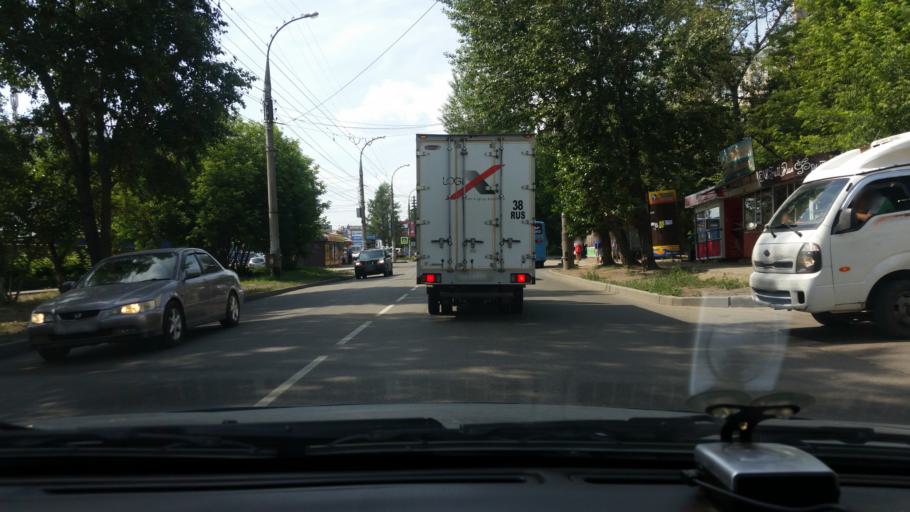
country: RU
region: Irkutsk
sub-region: Irkutskiy Rayon
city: Irkutsk
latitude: 52.2313
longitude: 104.3056
